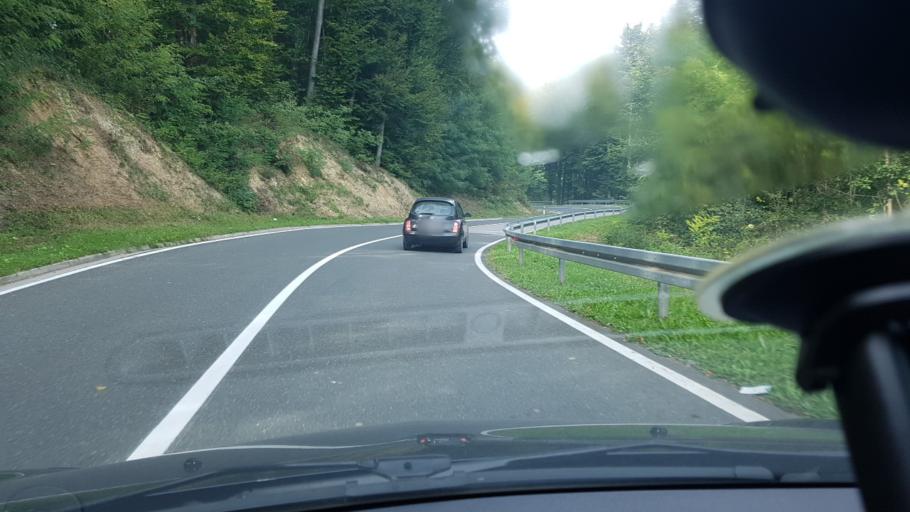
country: HR
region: Varazdinska
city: Ljubescica
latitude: 46.1344
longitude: 16.3591
